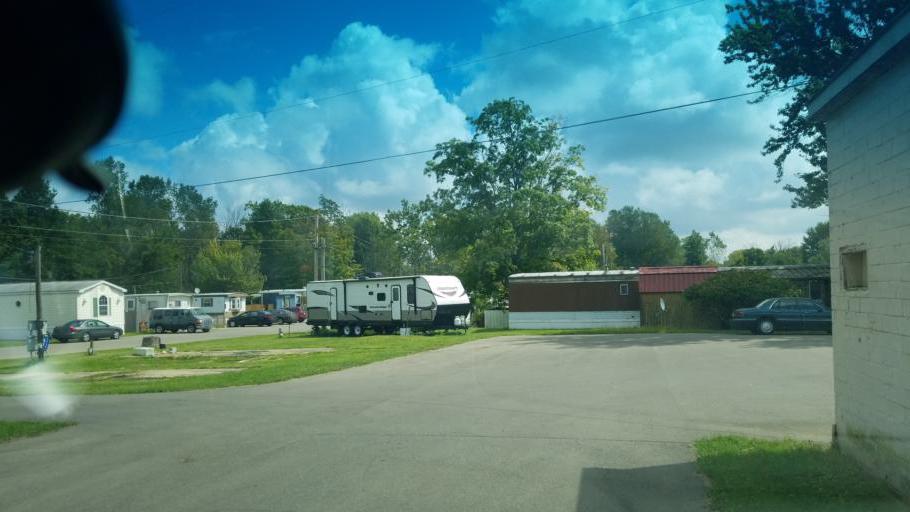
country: US
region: Ohio
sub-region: Crawford County
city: Galion
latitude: 40.7356
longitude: -82.8335
